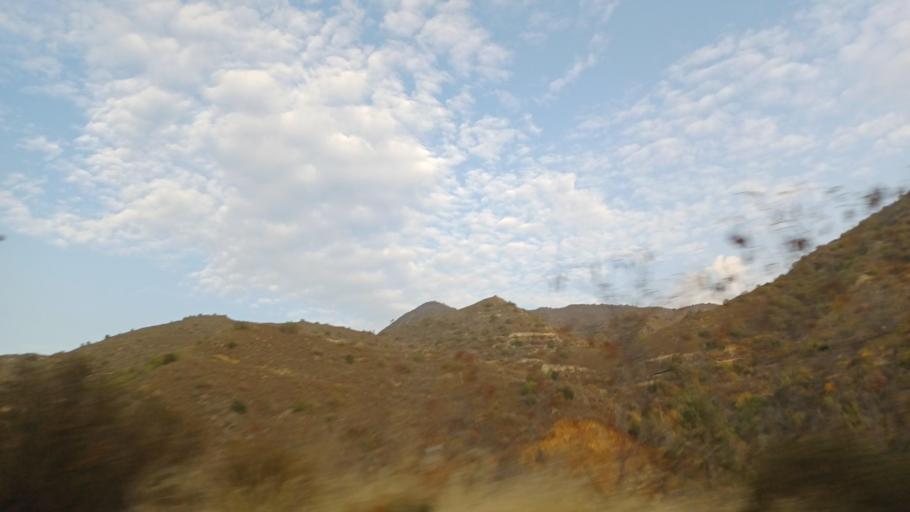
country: CY
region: Limassol
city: Pelendri
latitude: 34.8913
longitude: 32.9355
